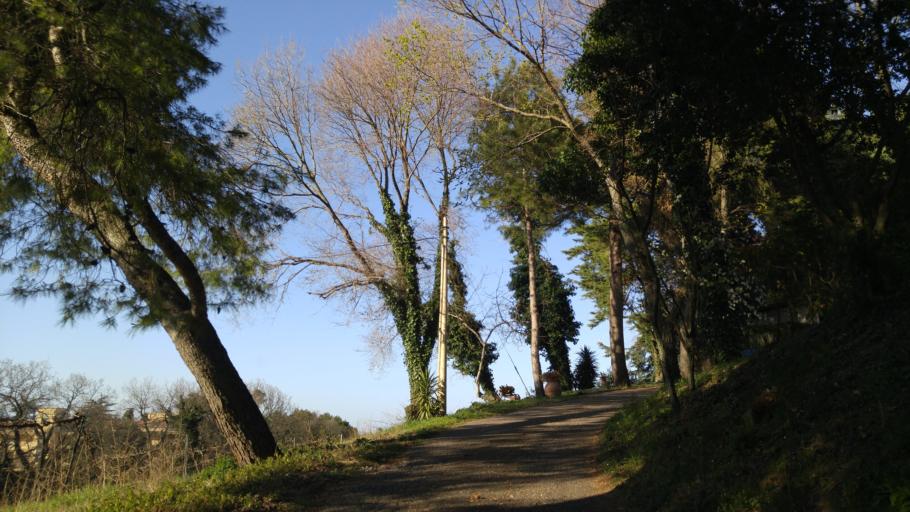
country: IT
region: The Marches
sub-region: Provincia di Pesaro e Urbino
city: Fenile
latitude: 43.8695
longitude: 12.9384
